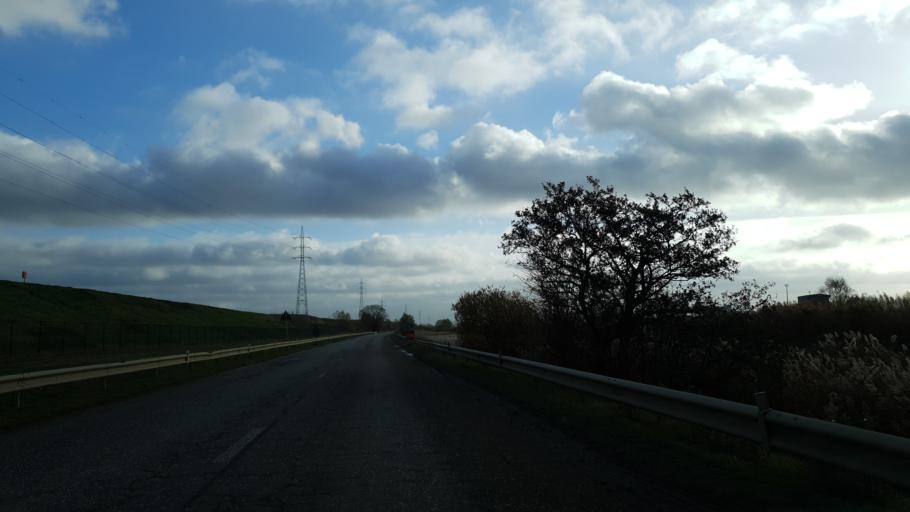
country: BE
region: Flanders
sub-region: Provincie Antwerpen
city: Stabroek
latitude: 51.3035
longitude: 4.3635
